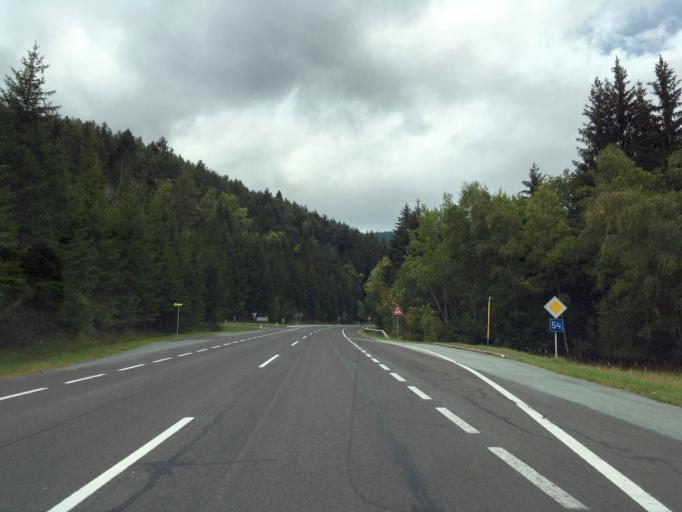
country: AT
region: Lower Austria
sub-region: Politischer Bezirk Neunkirchen
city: Monichkirchen
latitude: 47.5068
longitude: 16.0291
